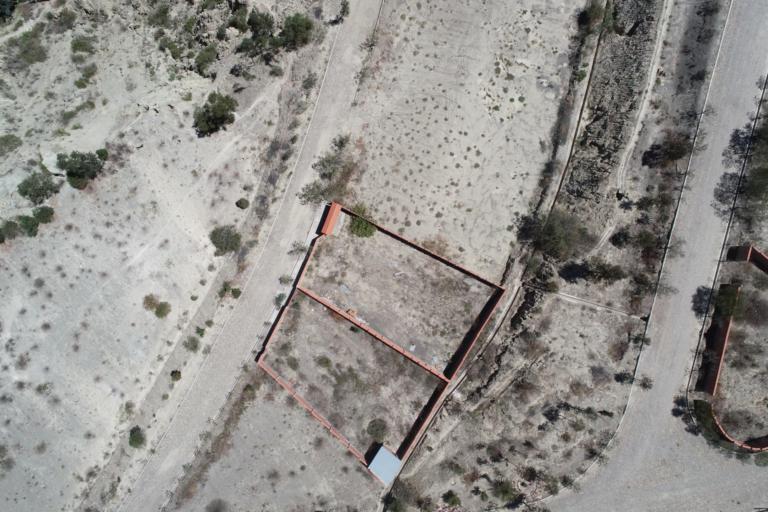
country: BO
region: La Paz
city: La Paz
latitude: -16.6290
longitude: -68.0582
